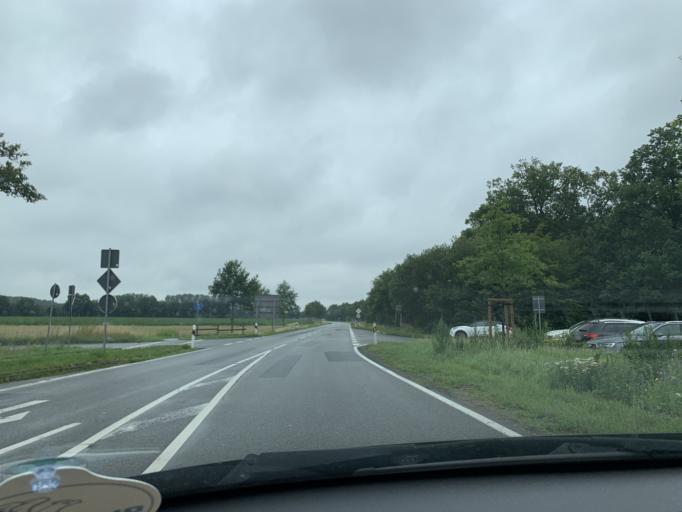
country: DE
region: North Rhine-Westphalia
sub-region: Regierungsbezirk Munster
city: Ochtrup
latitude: 52.1914
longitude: 7.2217
